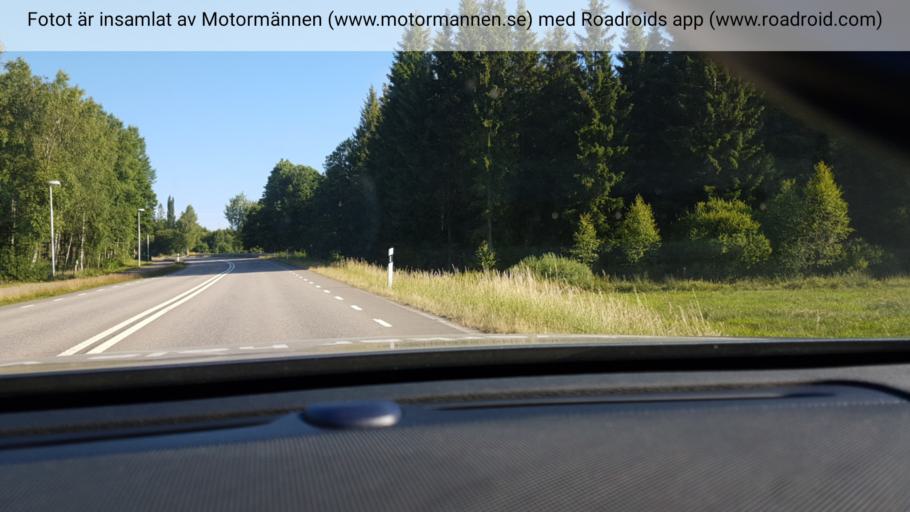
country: SE
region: Skane
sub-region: Hassleholms Kommun
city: Bjarnum
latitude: 56.3081
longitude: 13.6960
